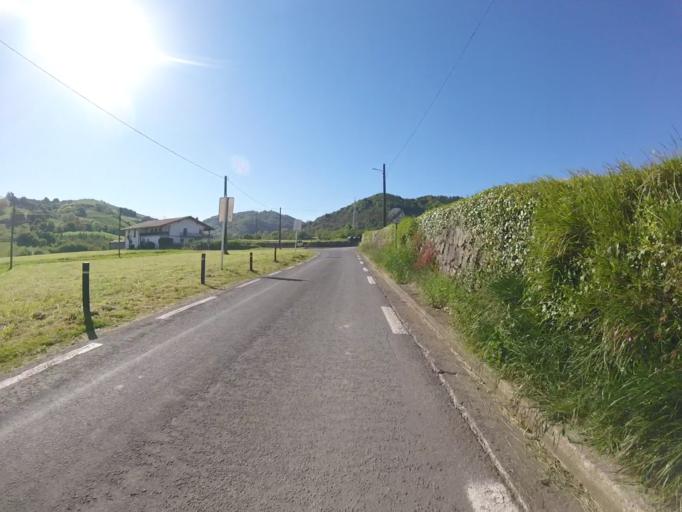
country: ES
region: Basque Country
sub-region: Provincia de Guipuzcoa
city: Aizarnazabal
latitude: 43.2333
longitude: -2.2246
